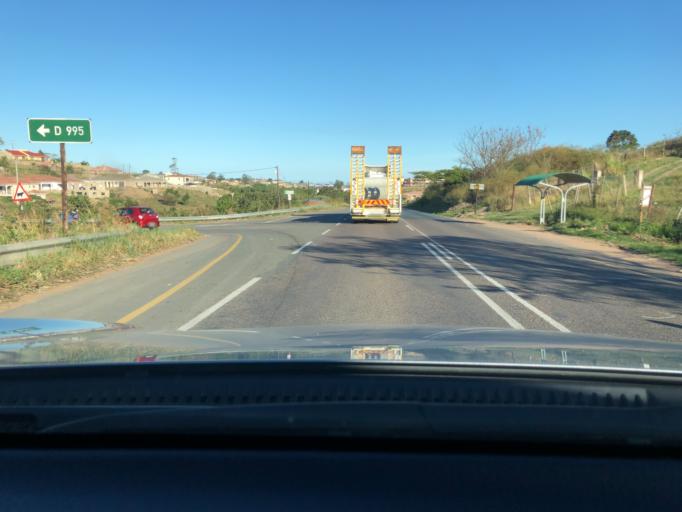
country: ZA
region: KwaZulu-Natal
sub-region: eThekwini Metropolitan Municipality
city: Umkomaas
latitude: -29.9986
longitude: 30.7985
